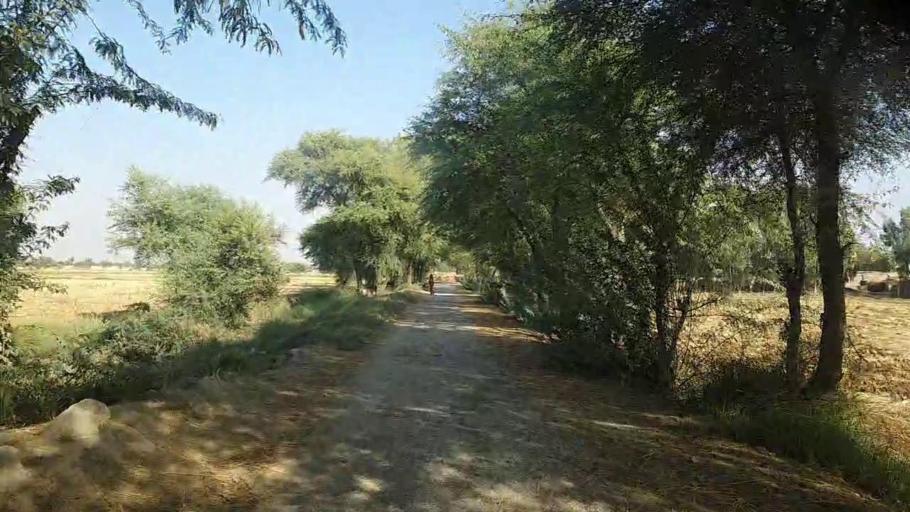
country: PK
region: Sindh
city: Tangwani
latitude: 28.2852
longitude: 68.9993
